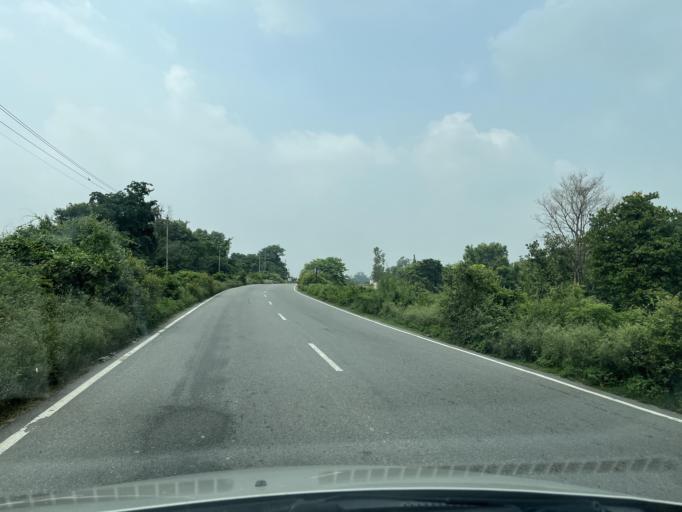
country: IN
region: Uttarakhand
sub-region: Haridwar
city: Sultanpur
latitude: 29.7624
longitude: 78.2738
